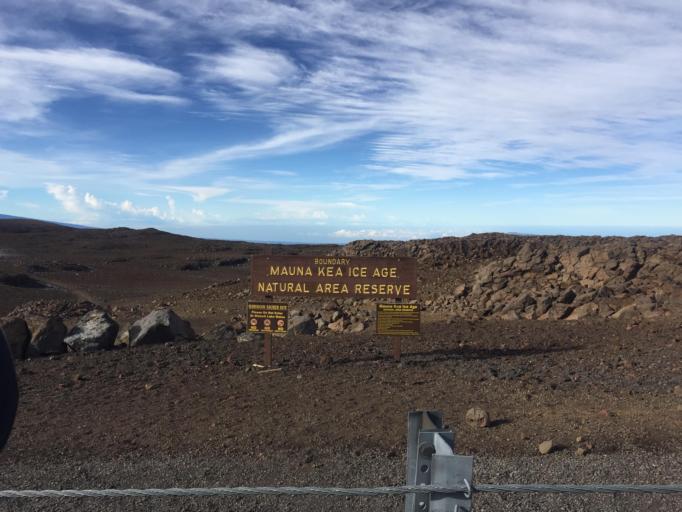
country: US
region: Hawaii
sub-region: Hawaii County
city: Honoka'a
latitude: 19.8185
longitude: -155.4736
